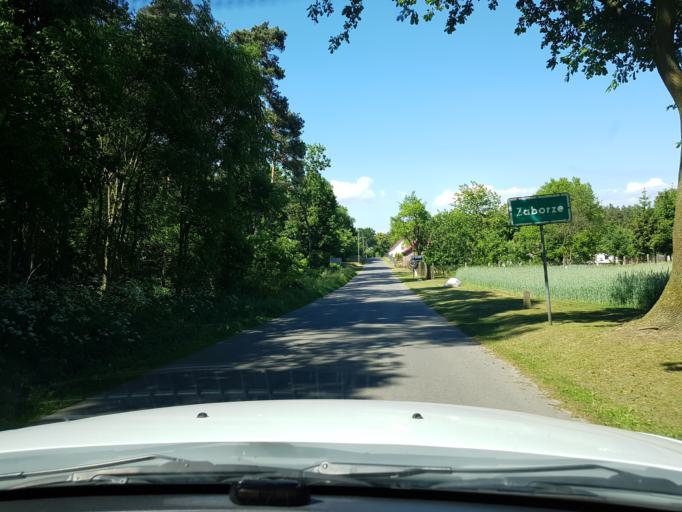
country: PL
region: West Pomeranian Voivodeship
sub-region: Powiat gryfinski
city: Gryfino
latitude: 53.1465
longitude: 14.5397
